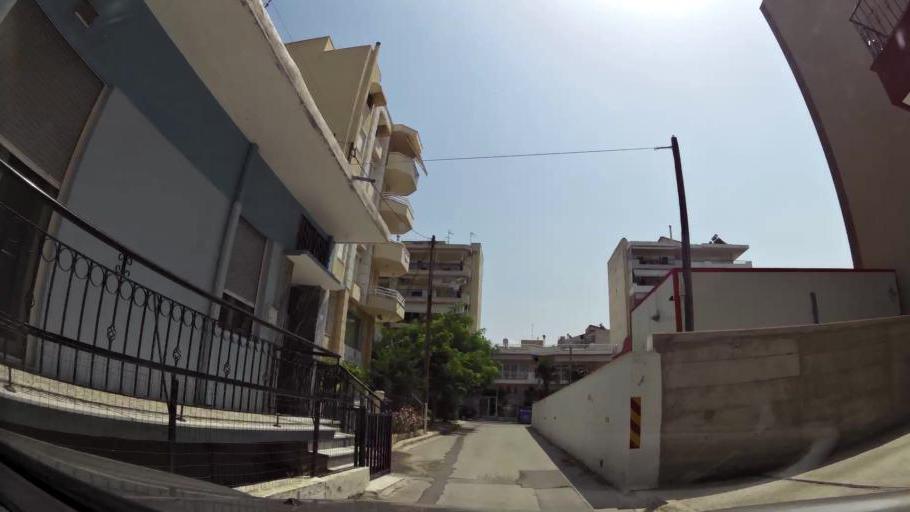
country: GR
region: Central Macedonia
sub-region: Nomos Thessalonikis
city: Evosmos
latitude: 40.6767
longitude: 22.9057
